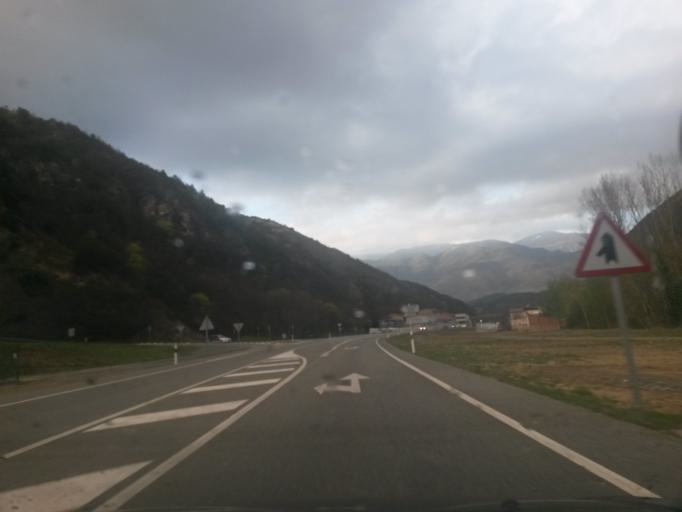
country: ES
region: Catalonia
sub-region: Provincia de Barcelona
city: Guardiola de Bergueda
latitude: 42.2169
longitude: 1.8690
